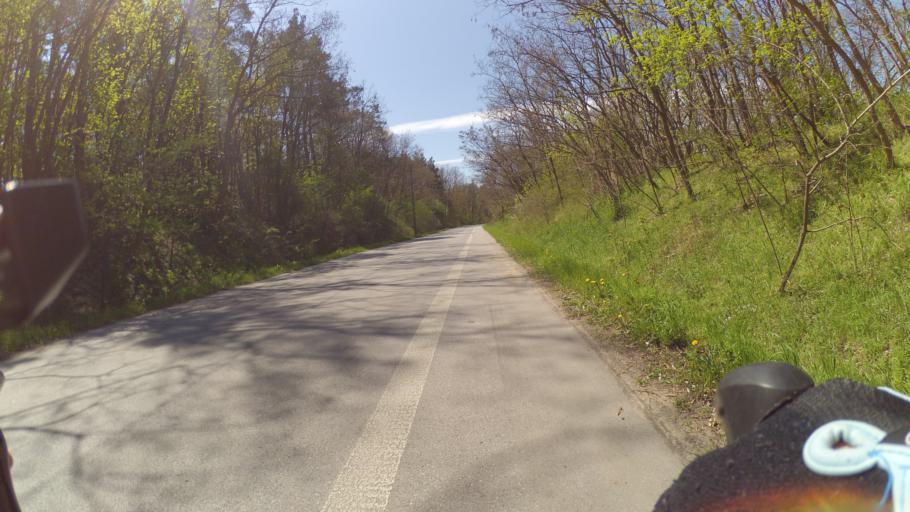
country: PL
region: Masovian Voivodeship
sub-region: Powiat nowodworski
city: Nowy Dwor Mazowiecki
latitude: 52.3925
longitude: 20.7194
